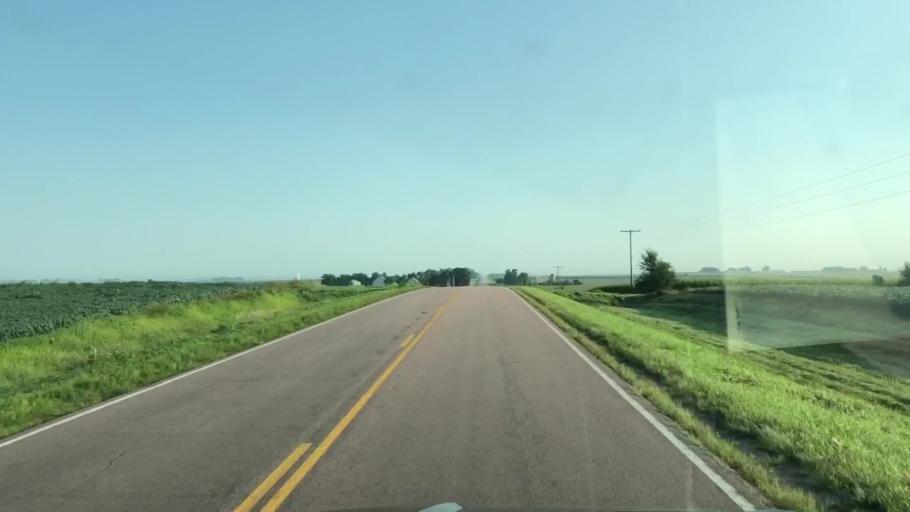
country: US
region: Iowa
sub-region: Lyon County
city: George
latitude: 43.2683
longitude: -95.9999
